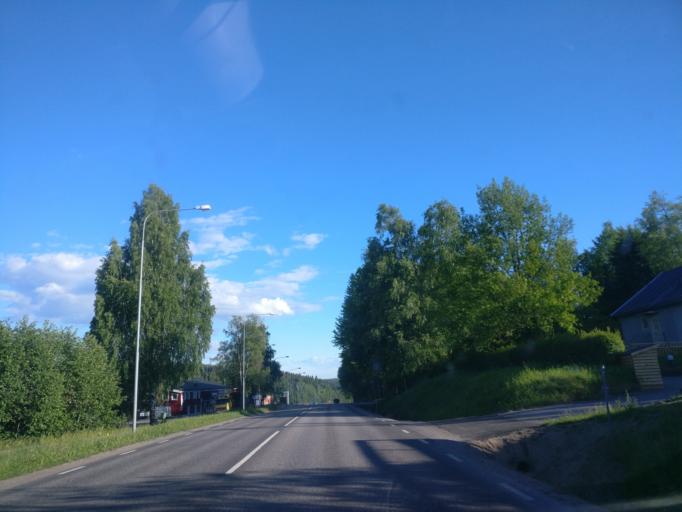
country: SE
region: Vaesternorrland
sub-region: Sundsvalls Kommun
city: Johannedal
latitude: 62.4275
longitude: 17.3467
